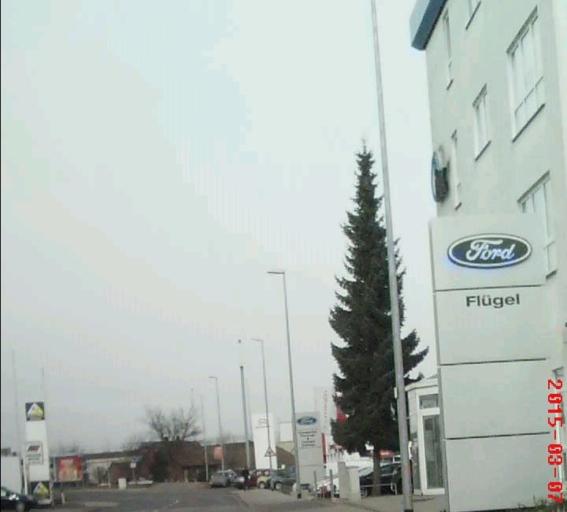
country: DE
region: Thuringia
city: Erfurt
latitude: 51.0107
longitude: 11.0158
